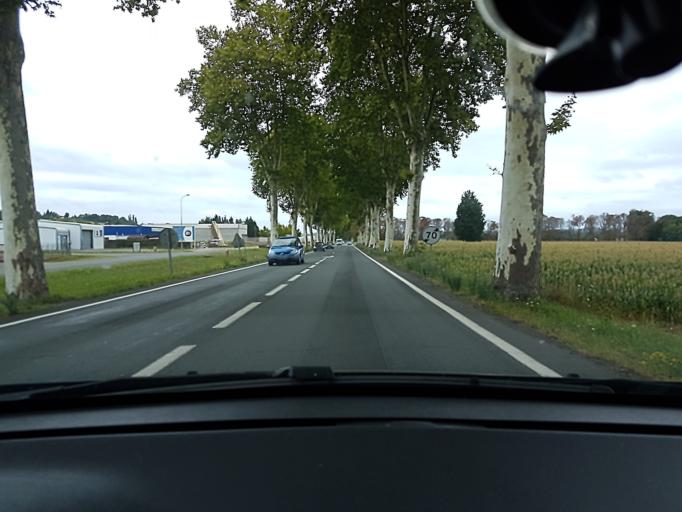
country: FR
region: Aquitaine
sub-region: Departement du Lot-et-Garonne
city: Nerac
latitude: 44.1494
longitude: 0.3240
